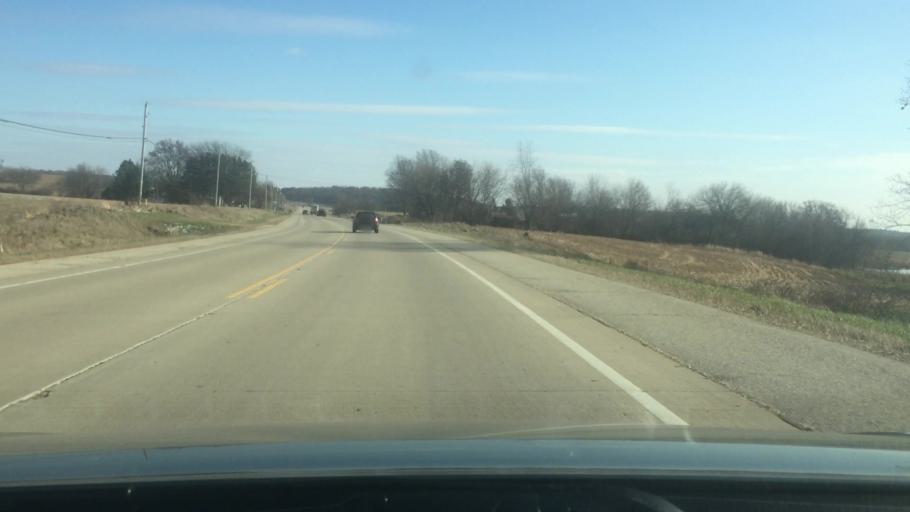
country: US
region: Wisconsin
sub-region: Jefferson County
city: Lake Ripley
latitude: 42.9782
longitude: -88.9602
